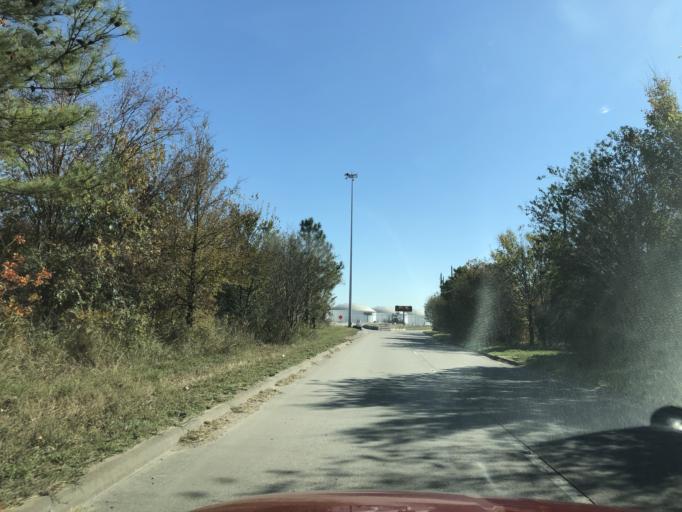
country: US
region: Texas
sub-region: Harris County
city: Cloverleaf
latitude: 29.7665
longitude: -95.1499
